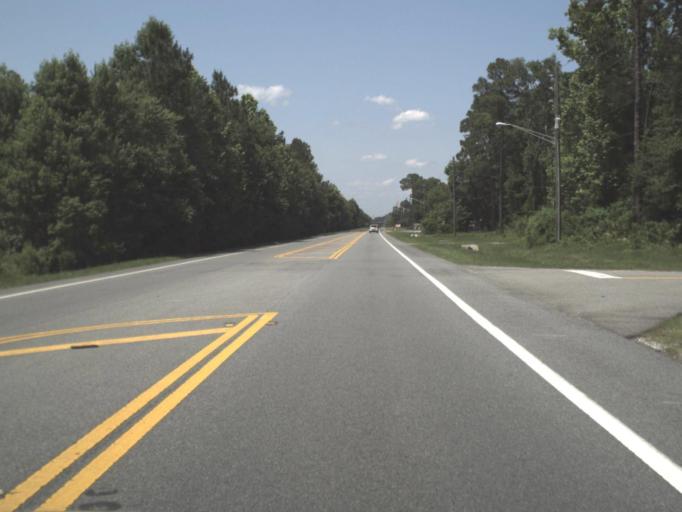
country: US
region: Florida
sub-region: Nassau County
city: Yulee
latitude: 30.5050
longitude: -81.6229
